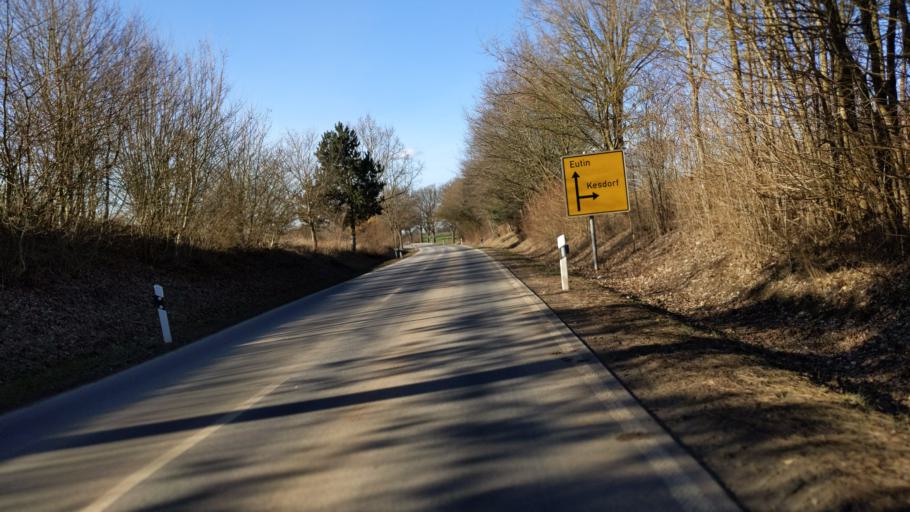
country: DE
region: Schleswig-Holstein
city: Susel
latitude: 54.0623
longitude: 10.6475
